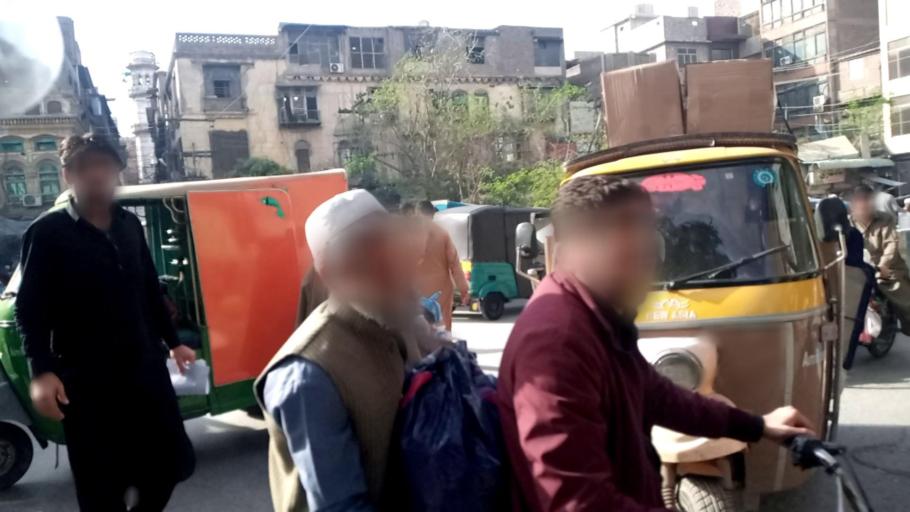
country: PK
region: Khyber Pakhtunkhwa
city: Peshawar
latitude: 34.0102
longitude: 71.5745
